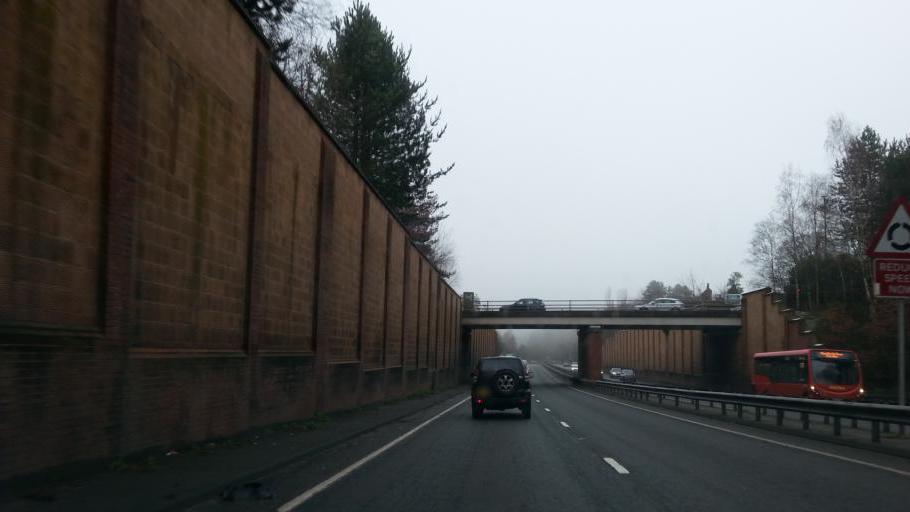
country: GB
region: England
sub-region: Cheshire East
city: Wilmslow
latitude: 53.3253
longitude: -2.2254
